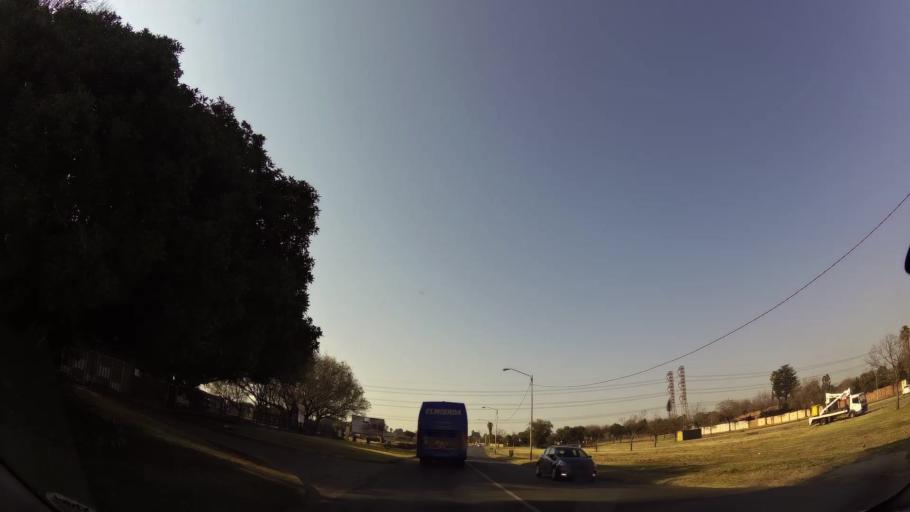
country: ZA
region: Gauteng
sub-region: City of Johannesburg Metropolitan Municipality
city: Modderfontein
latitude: -26.1424
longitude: 28.1916
